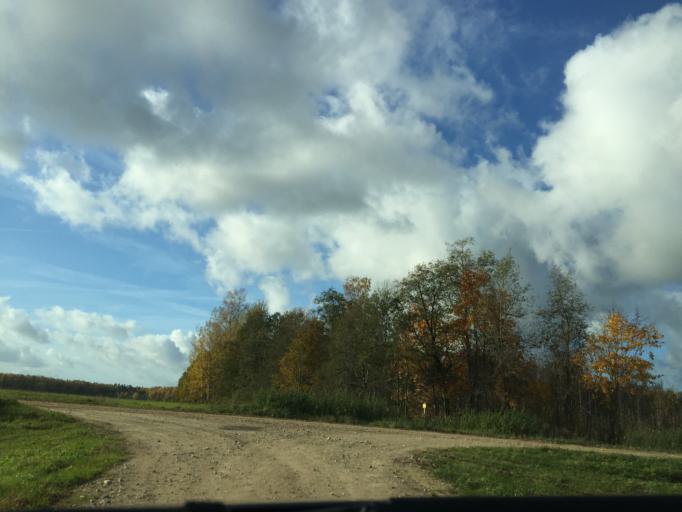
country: LV
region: Lielvarde
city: Lielvarde
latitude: 56.7394
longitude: 24.9003
